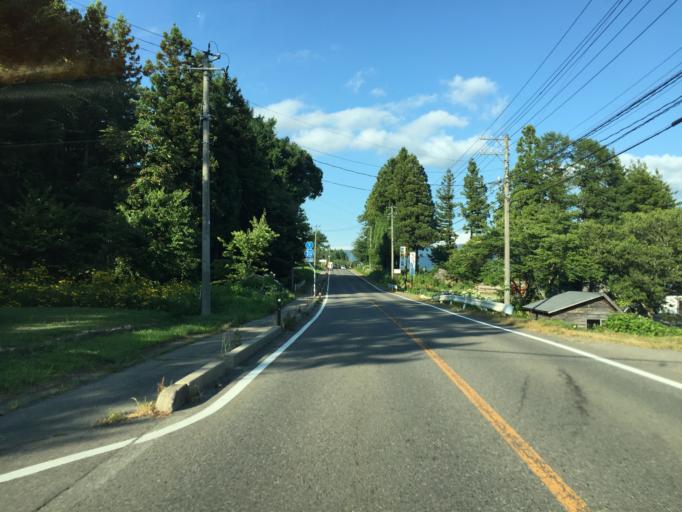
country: JP
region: Fukushima
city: Inawashiro
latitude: 37.5574
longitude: 140.0818
